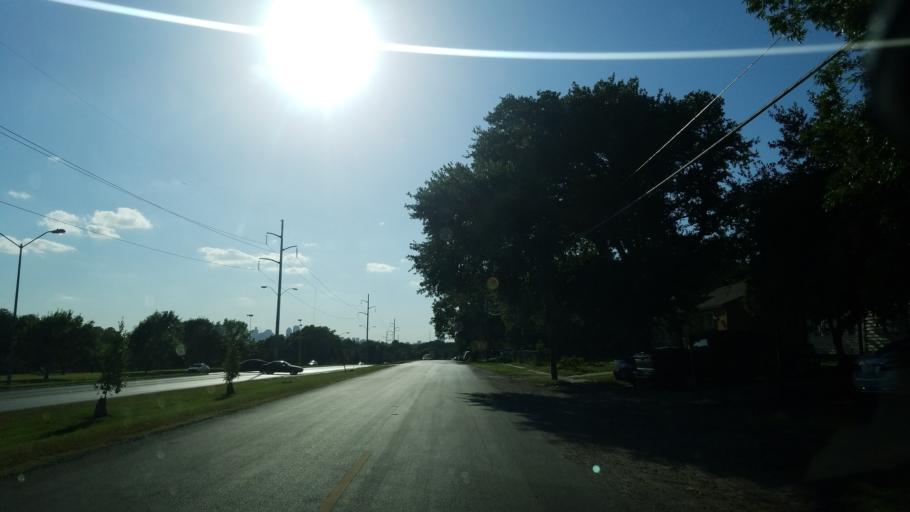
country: US
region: Texas
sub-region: Dallas County
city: Dallas
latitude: 32.7759
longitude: -96.7132
